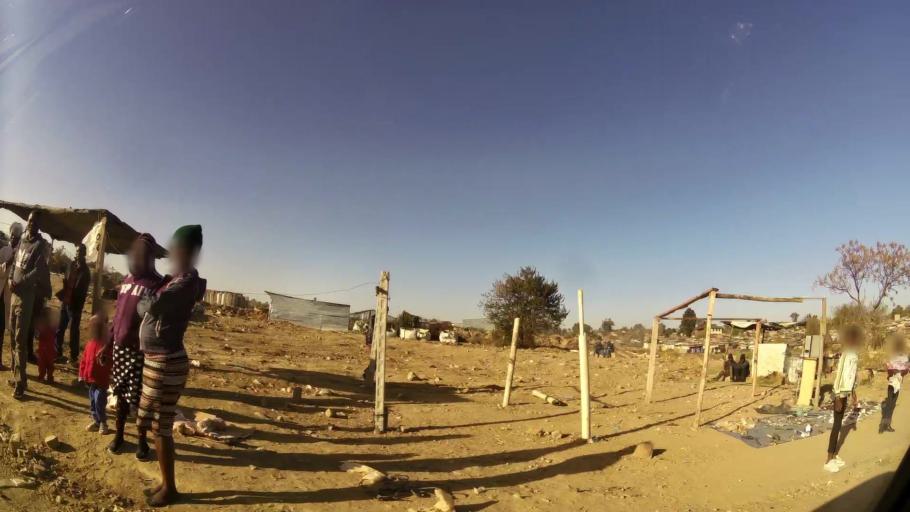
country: ZA
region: Gauteng
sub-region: City of Johannesburg Metropolitan Municipality
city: Diepsloot
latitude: -25.9277
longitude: 28.0120
